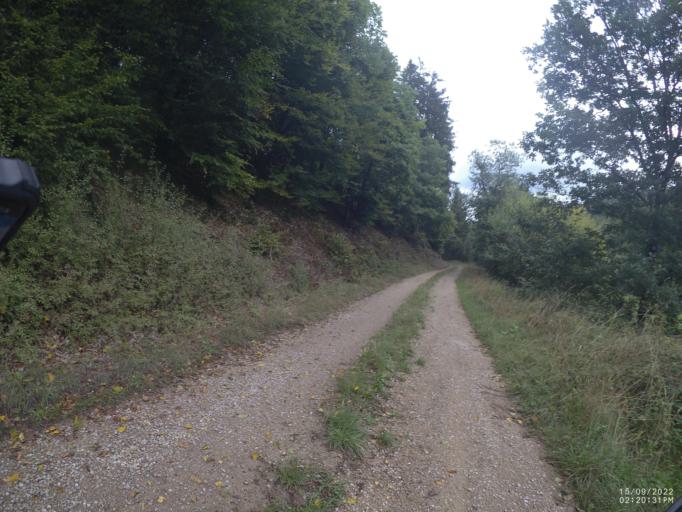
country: DE
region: Rheinland-Pfalz
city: Oberehe-Stroheich
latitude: 50.2926
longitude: 6.7844
